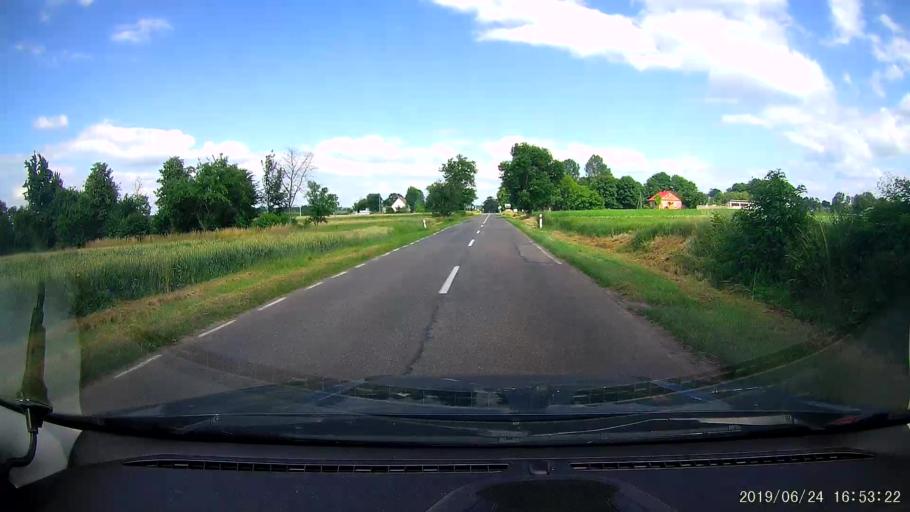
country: PL
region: Lublin Voivodeship
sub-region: Powiat tomaszowski
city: Telatyn
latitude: 50.5354
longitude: 23.7998
